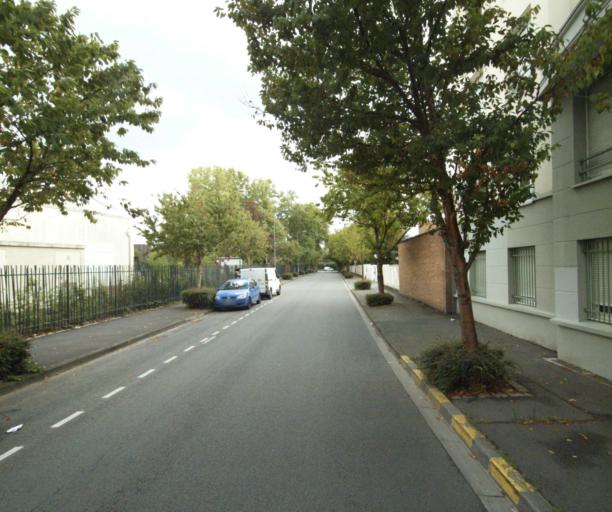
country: FR
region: Nord-Pas-de-Calais
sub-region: Departement du Nord
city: La Madeleine
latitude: 50.6476
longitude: 3.0638
